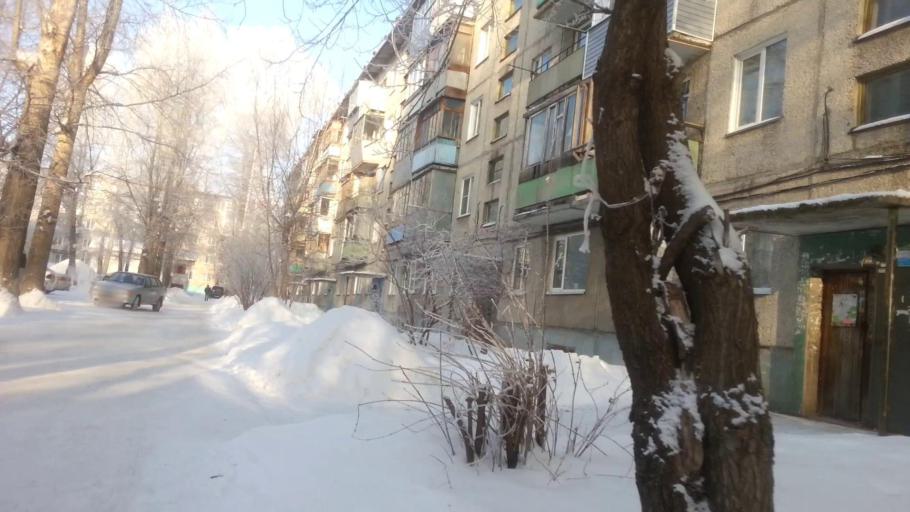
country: RU
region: Altai Krai
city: Novosilikatnyy
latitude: 53.3766
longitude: 83.6727
